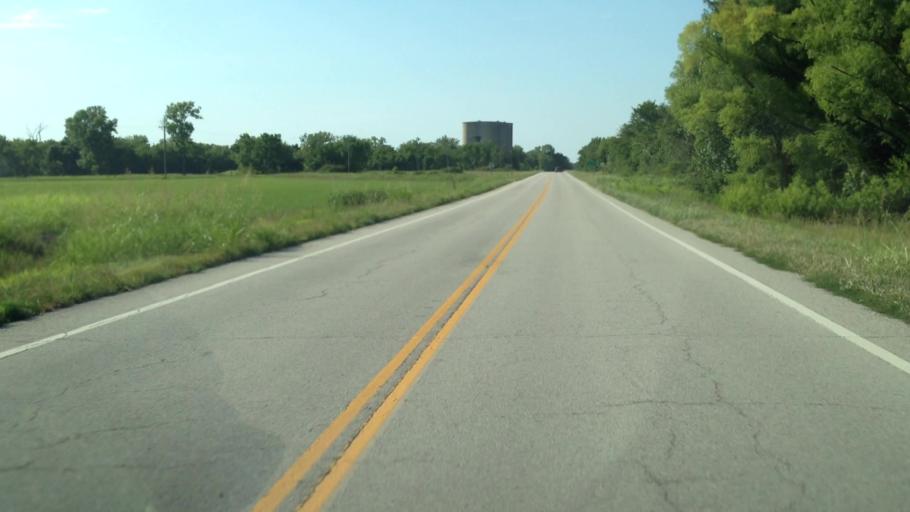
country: US
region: Kansas
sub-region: Allen County
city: Iola
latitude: 38.0240
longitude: -95.1715
